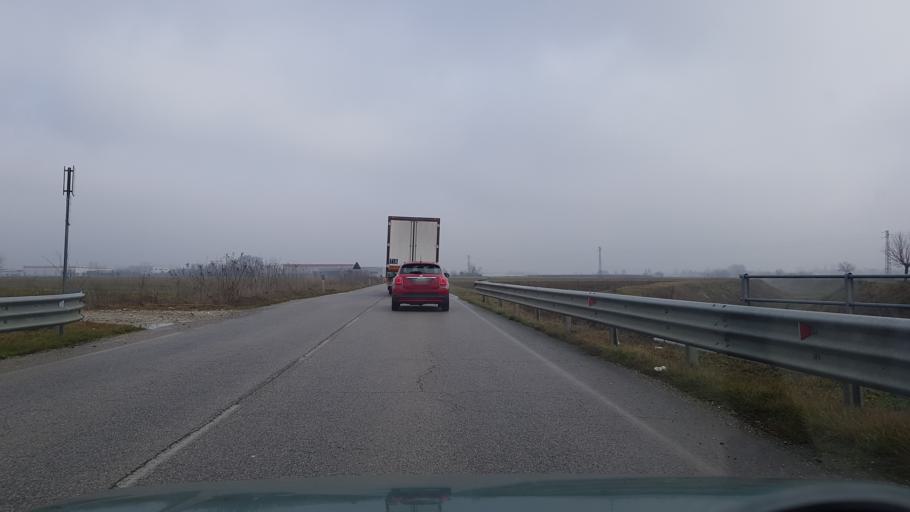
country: IT
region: Friuli Venezia Giulia
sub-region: Provincia di Udine
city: Ialmicco
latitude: 45.9166
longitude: 13.3571
